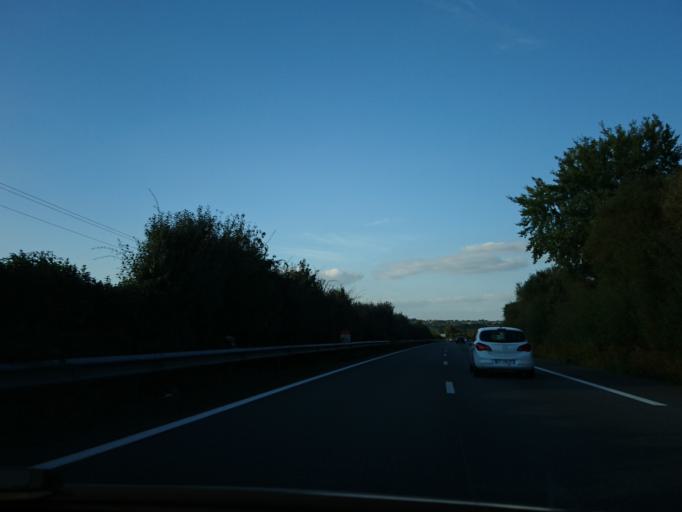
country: FR
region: Brittany
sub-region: Departement d'Ille-et-Vilaine
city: Grand-Fougeray
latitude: 47.6934
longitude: -1.7032
